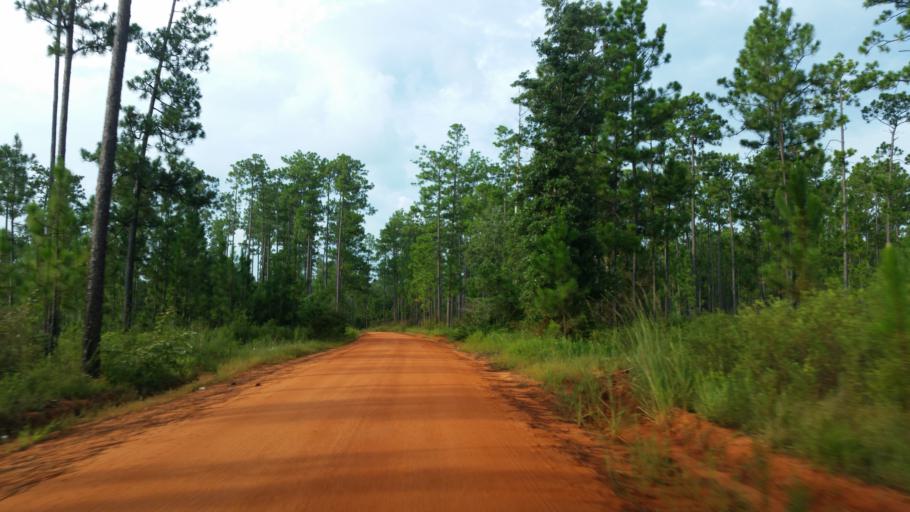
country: US
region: Alabama
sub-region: Escambia County
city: Atmore
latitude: 30.8797
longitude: -87.5829
